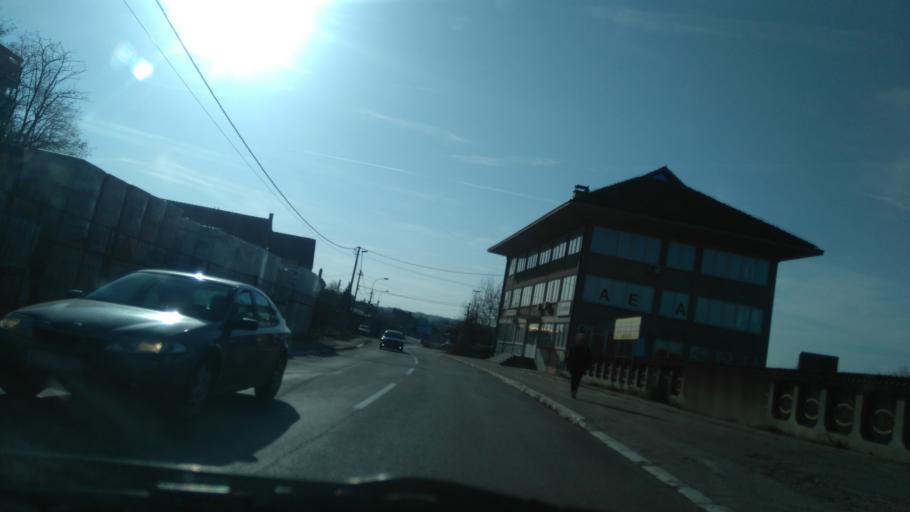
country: RS
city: Ostruznica
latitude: 44.7309
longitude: 20.3680
